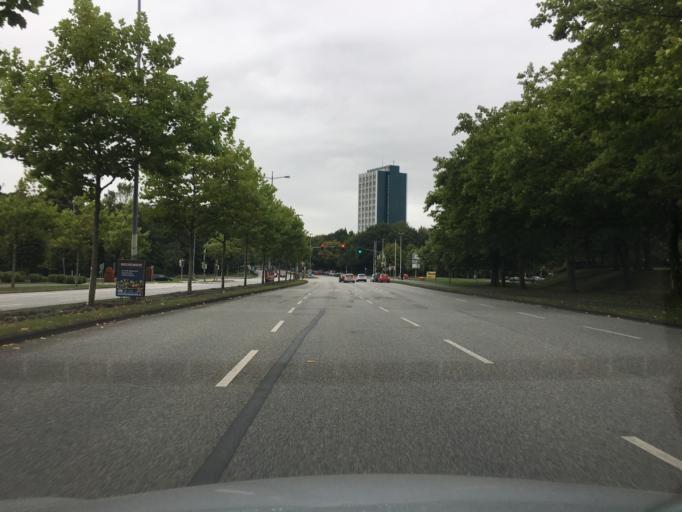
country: DE
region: Schleswig-Holstein
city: Kiel
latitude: 54.3144
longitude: 10.1099
